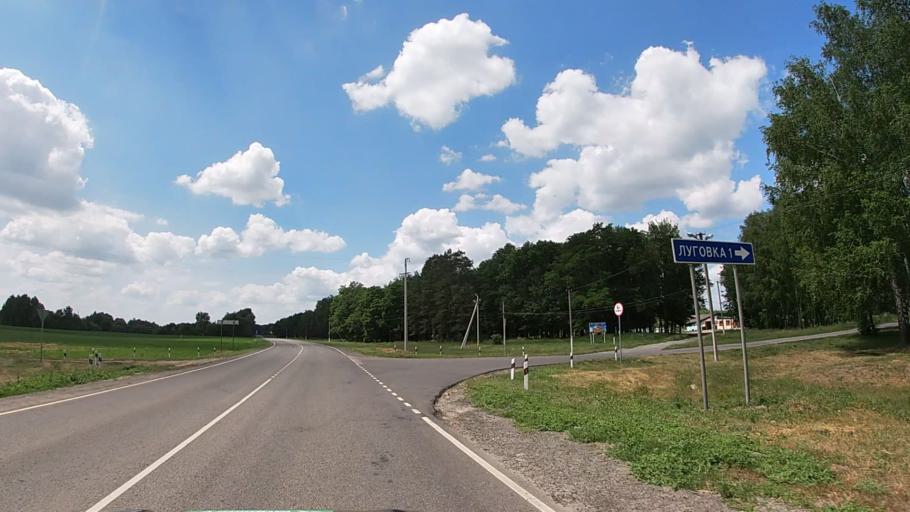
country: RU
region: Belgorod
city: Grayvoron
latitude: 50.5005
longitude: 35.7236
